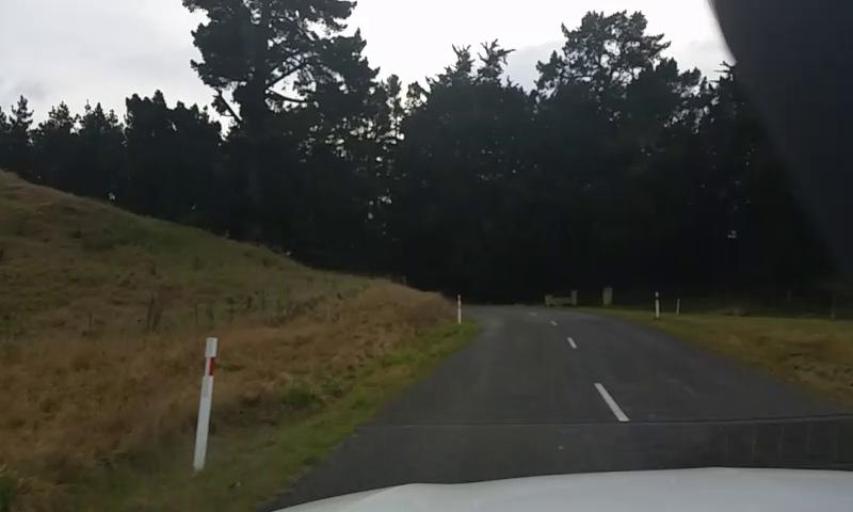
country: NZ
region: Canterbury
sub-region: Waimakariri District
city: Kaiapoi
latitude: -43.2985
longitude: 172.4379
